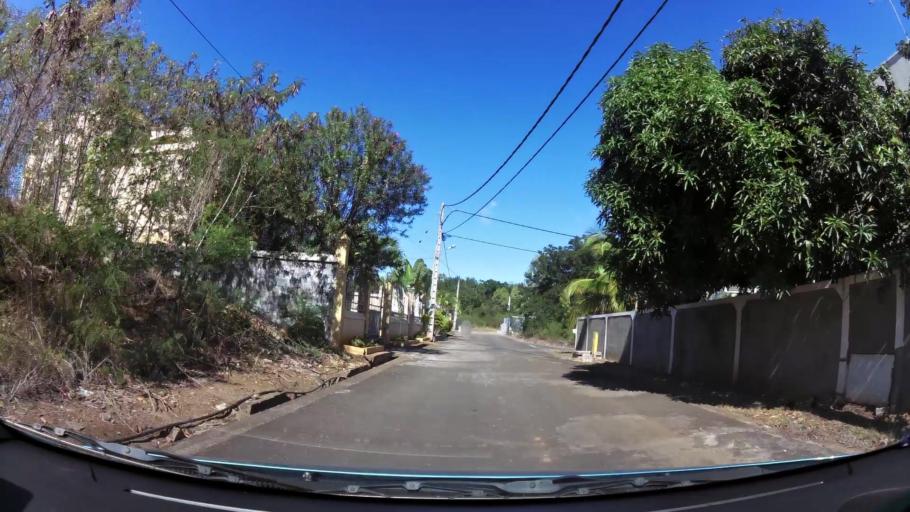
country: MU
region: Black River
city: Flic en Flac
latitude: -20.2849
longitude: 57.3731
